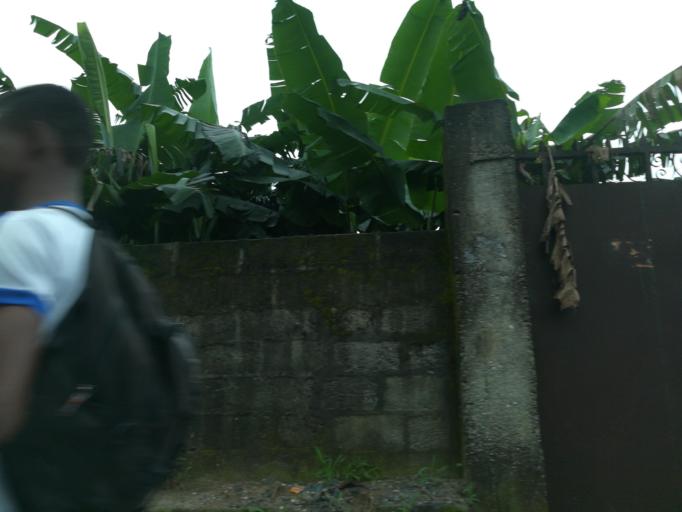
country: NG
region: Rivers
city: Port Harcourt
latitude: 4.8605
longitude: 7.0356
